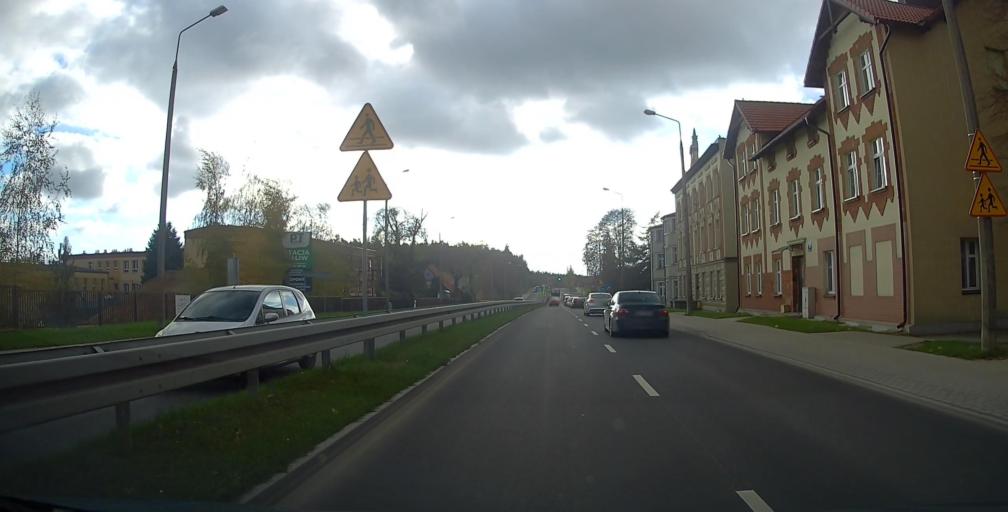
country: PL
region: Warmian-Masurian Voivodeship
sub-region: Powiat elcki
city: Elk
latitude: 53.8042
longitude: 22.3662
